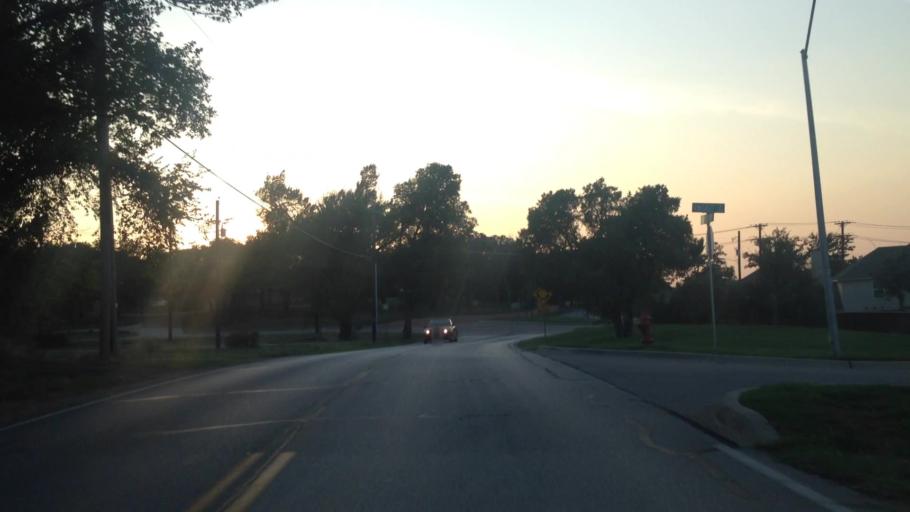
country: US
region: Texas
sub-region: Tarrant County
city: Kennedale
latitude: 32.6382
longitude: -97.2075
